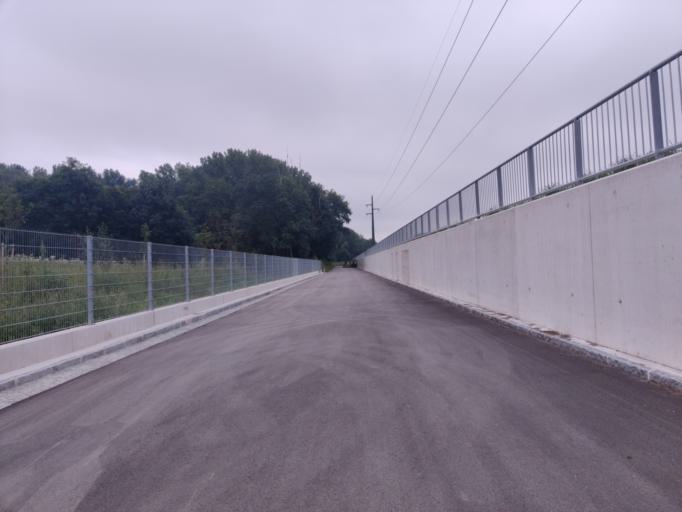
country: AT
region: Lower Austria
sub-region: Politischer Bezirk Krems
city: Gedersdorf
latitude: 48.3983
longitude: 15.6665
